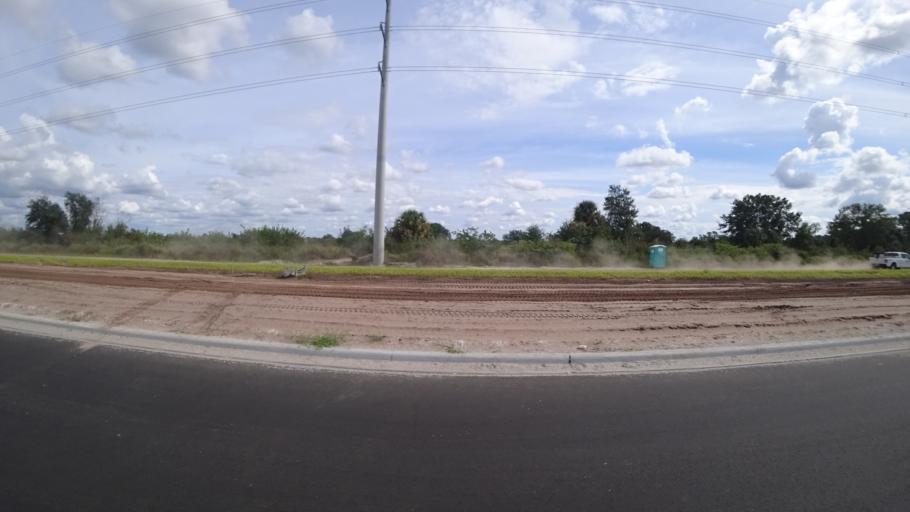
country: US
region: Florida
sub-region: Sarasota County
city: The Meadows
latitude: 27.4605
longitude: -82.3510
